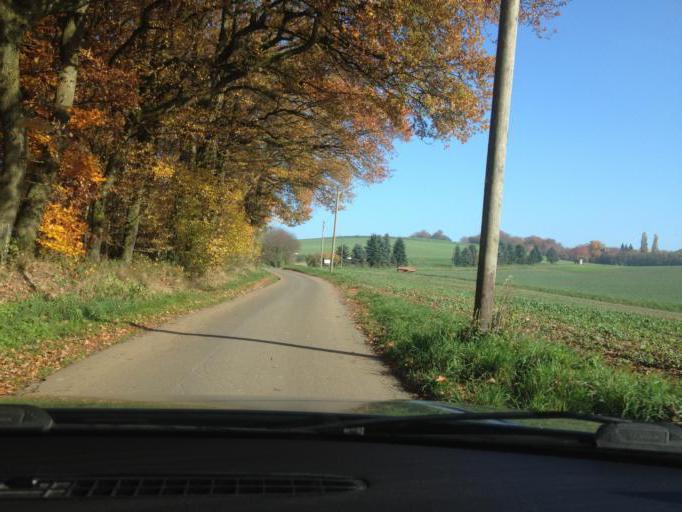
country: DE
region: Saarland
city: Sankt Wendel
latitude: 49.5006
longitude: 7.1995
